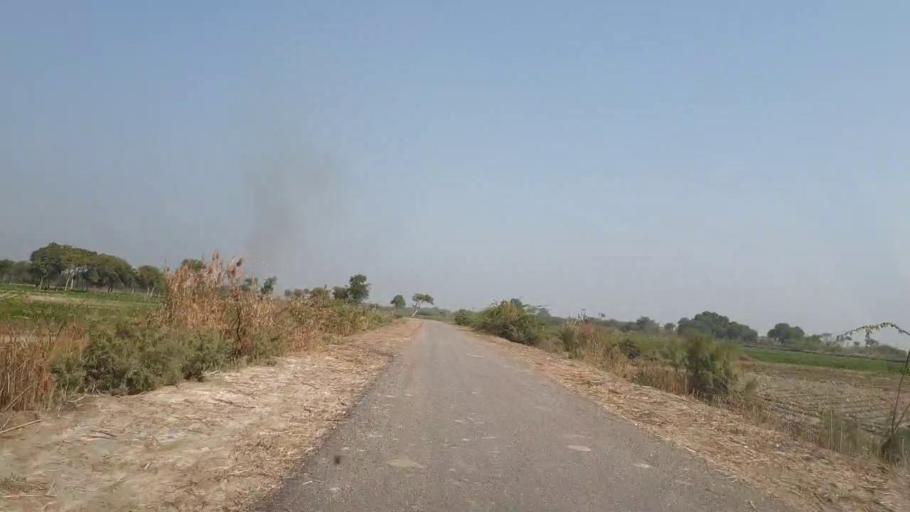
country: PK
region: Sindh
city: Mirpur Khas
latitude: 25.5881
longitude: 69.0027
